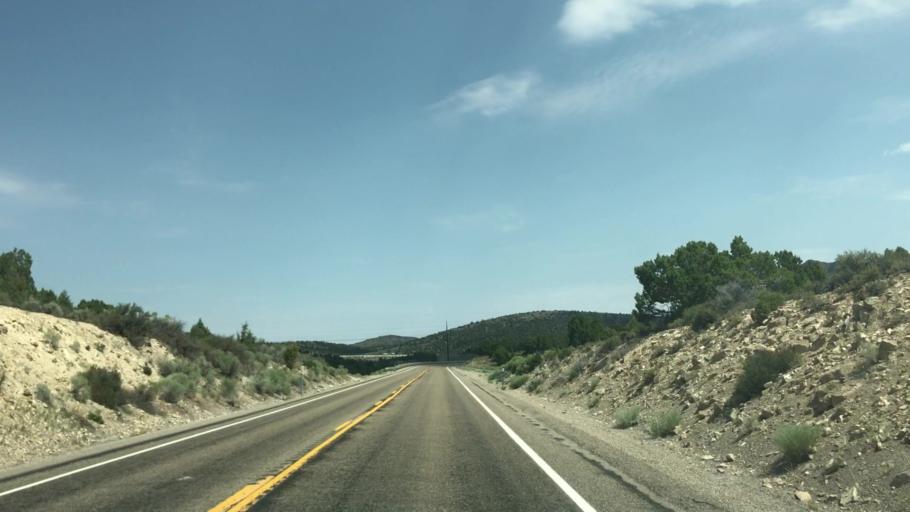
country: US
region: Nevada
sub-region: White Pine County
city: Ely
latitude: 39.3994
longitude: -115.0830
